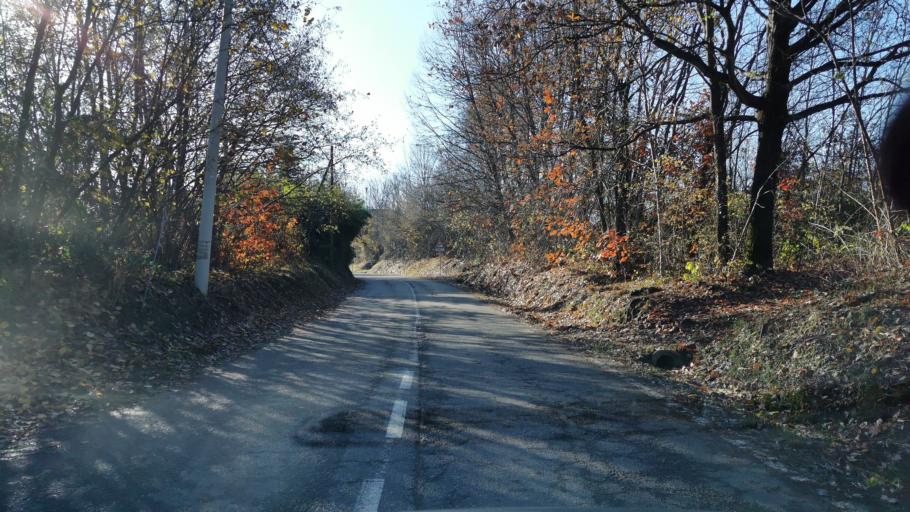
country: IT
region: Piedmont
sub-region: Provincia di Torino
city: Fiano
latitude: 45.2060
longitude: 7.5273
